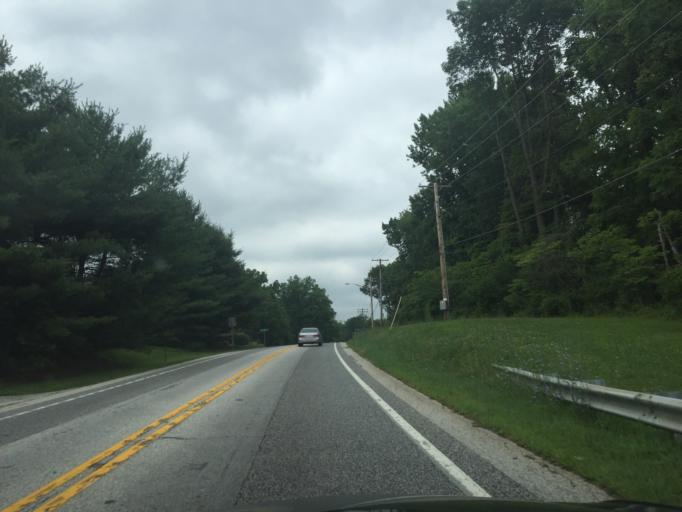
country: US
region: Maryland
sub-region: Baltimore County
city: Timonium
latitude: 39.4441
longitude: -76.5965
